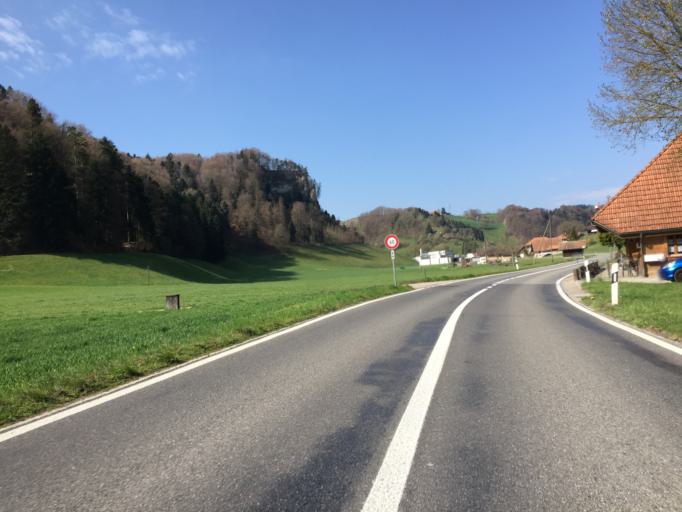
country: CH
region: Bern
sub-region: Emmental District
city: Krauchthal
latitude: 47.0003
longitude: 7.5472
